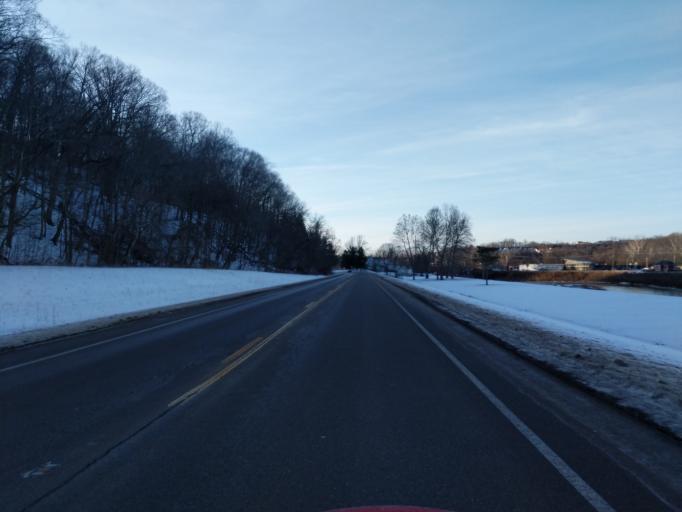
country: US
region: Ohio
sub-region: Athens County
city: Athens
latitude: 39.3278
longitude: -82.1215
